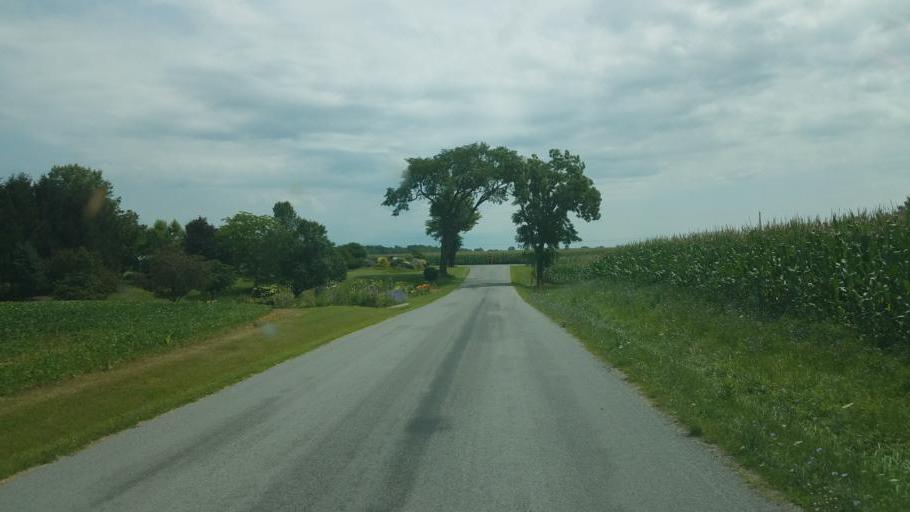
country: US
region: Ohio
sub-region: Wyandot County
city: Upper Sandusky
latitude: 40.8656
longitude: -83.2245
